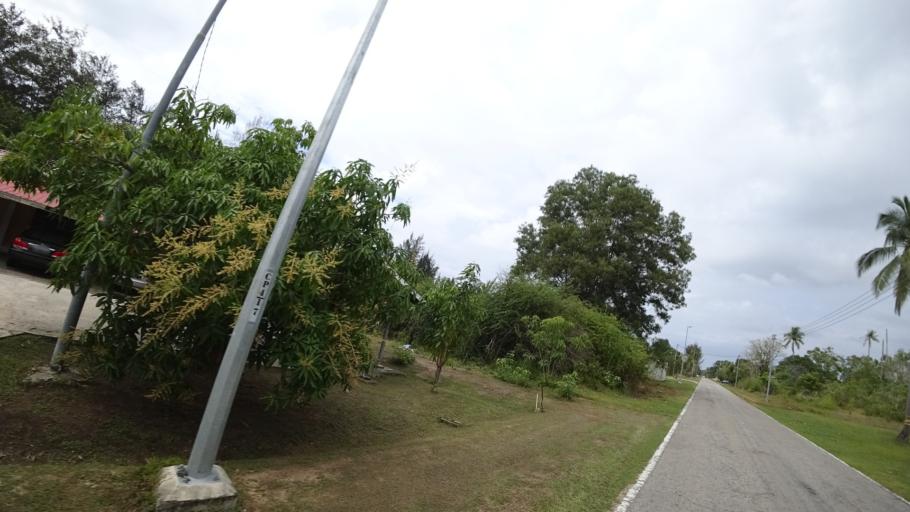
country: BN
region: Tutong
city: Tutong
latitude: 4.7789
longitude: 114.6055
